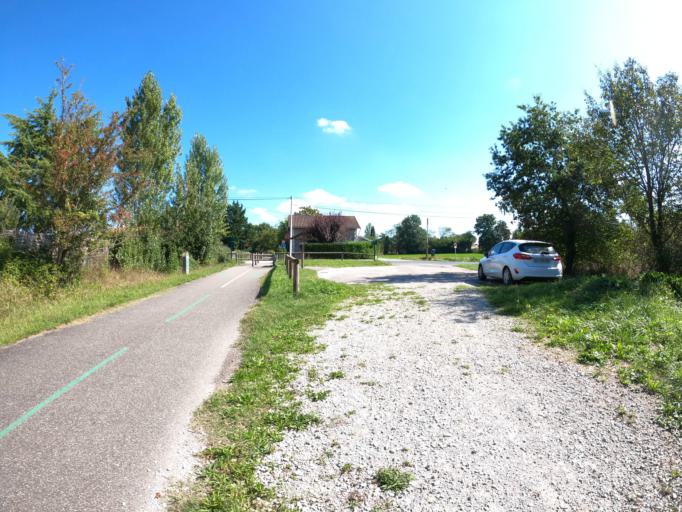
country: FR
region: Aquitaine
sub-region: Departement du Lot-et-Garonne
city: Bias
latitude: 44.4013
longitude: 0.6706
